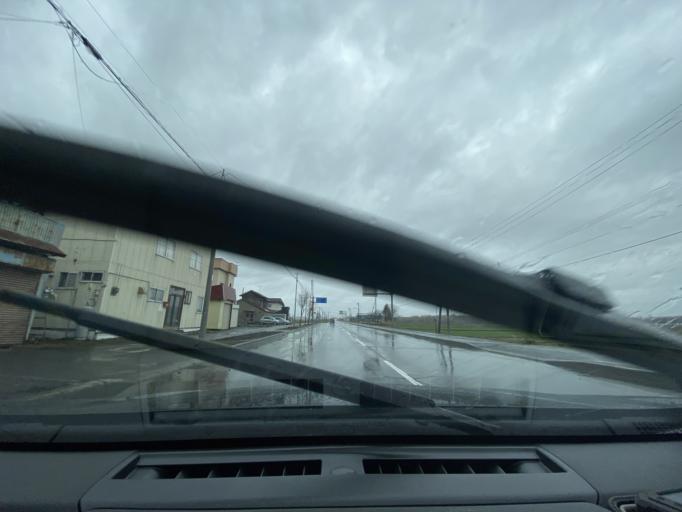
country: JP
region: Hokkaido
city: Fukagawa
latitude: 43.8090
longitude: 142.0219
